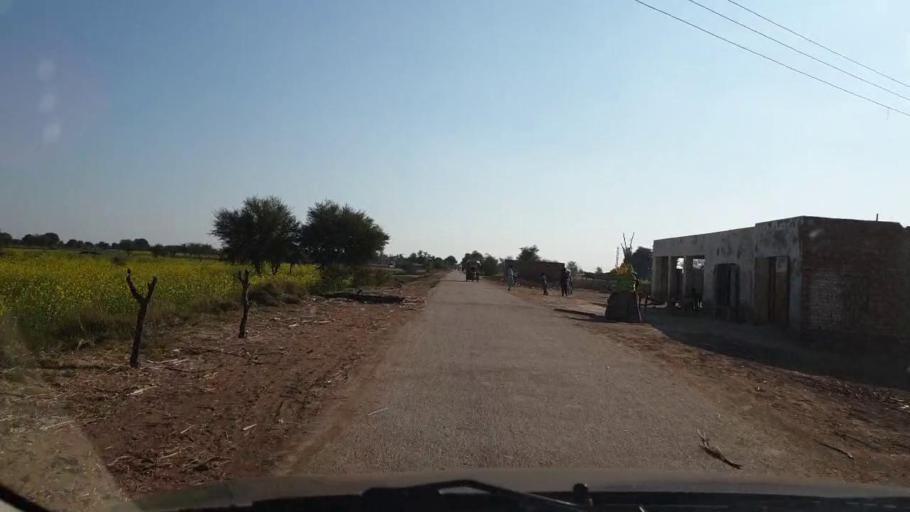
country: PK
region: Sindh
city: Jhol
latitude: 25.9796
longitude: 68.8395
